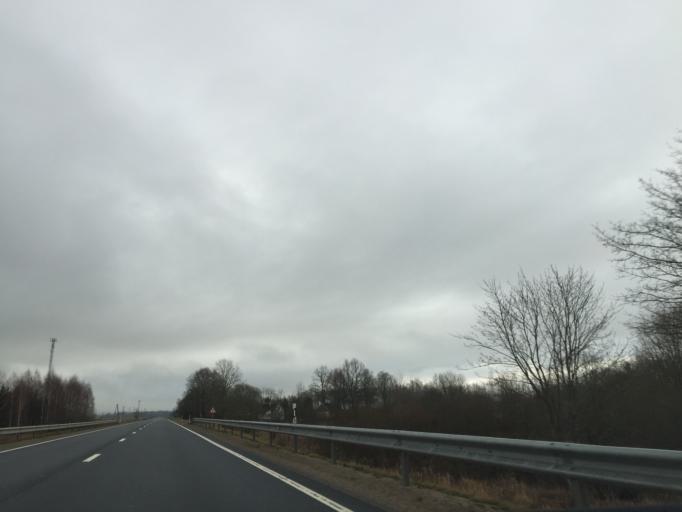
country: LV
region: Durbe
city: Liegi
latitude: 56.5911
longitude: 21.3907
